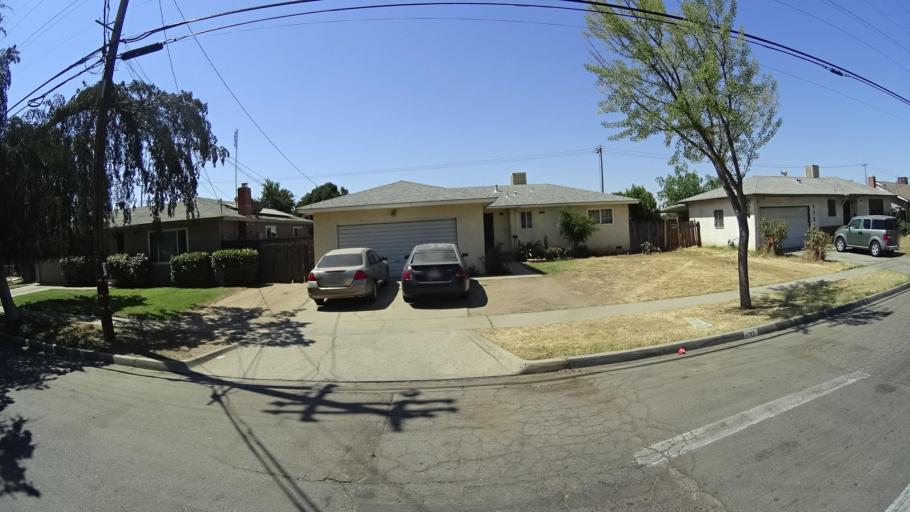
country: US
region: California
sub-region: Fresno County
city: Fresno
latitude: 36.7219
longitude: -119.7381
